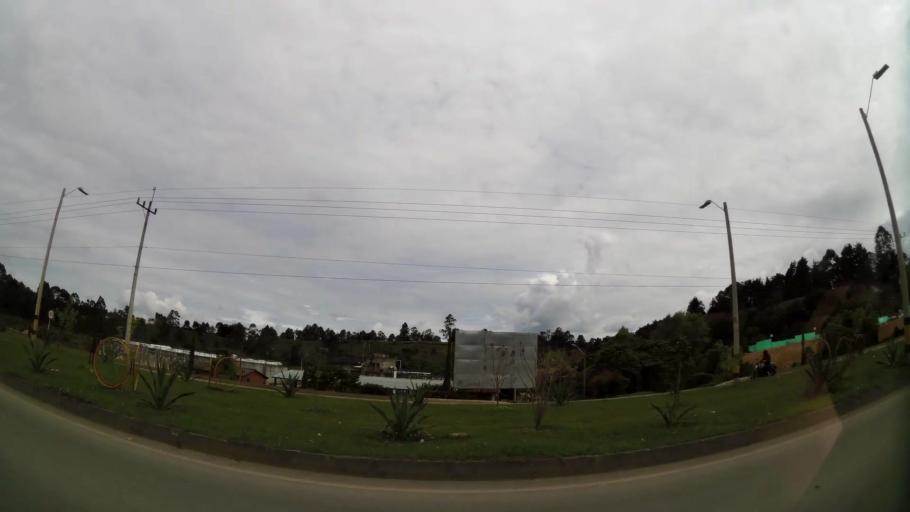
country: CO
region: Antioquia
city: Rionegro
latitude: 6.1624
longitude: -75.3637
